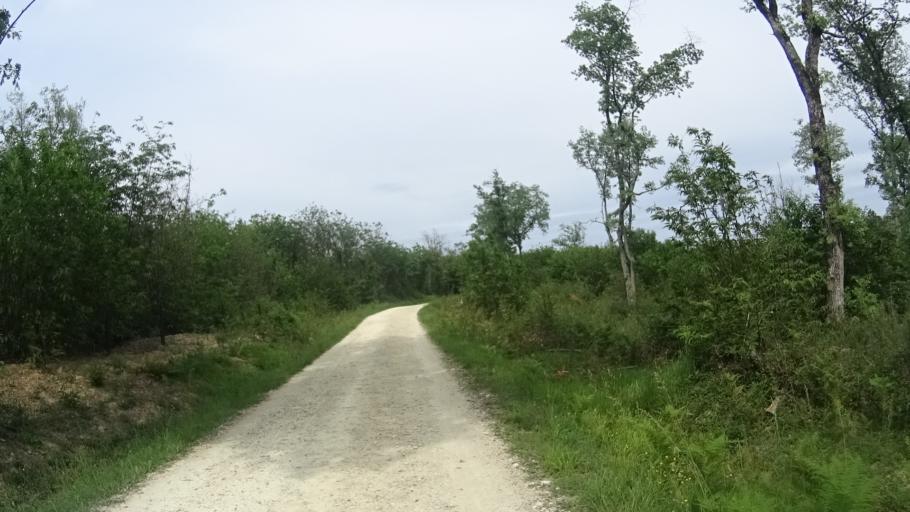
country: FR
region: Aquitaine
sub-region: Departement de la Dordogne
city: Neuvic
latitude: 45.0077
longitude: 0.5515
